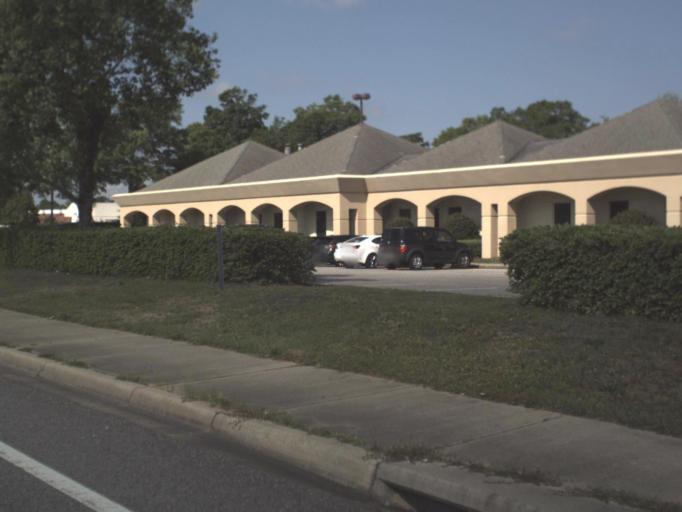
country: US
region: Florida
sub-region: Escambia County
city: Ferry Pass
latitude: 30.5129
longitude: -87.2189
